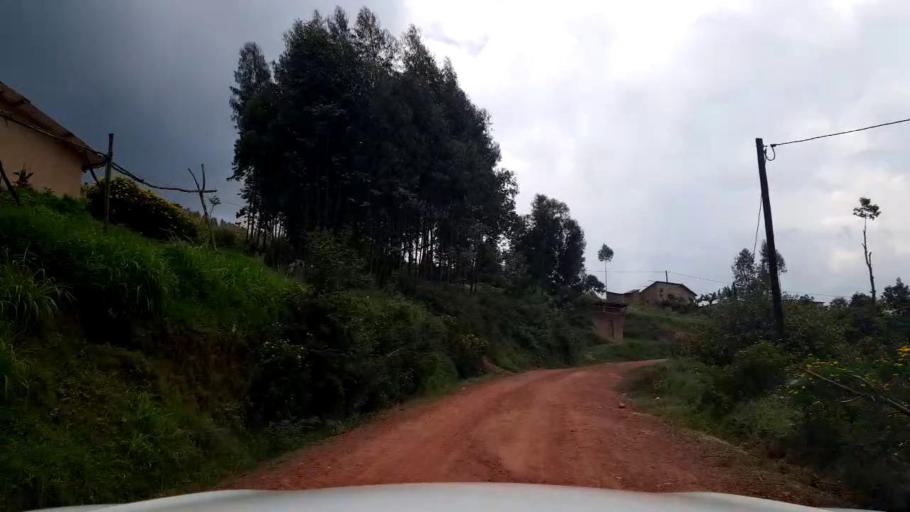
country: RW
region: Northern Province
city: Byumba
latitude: -1.4826
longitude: 29.9194
